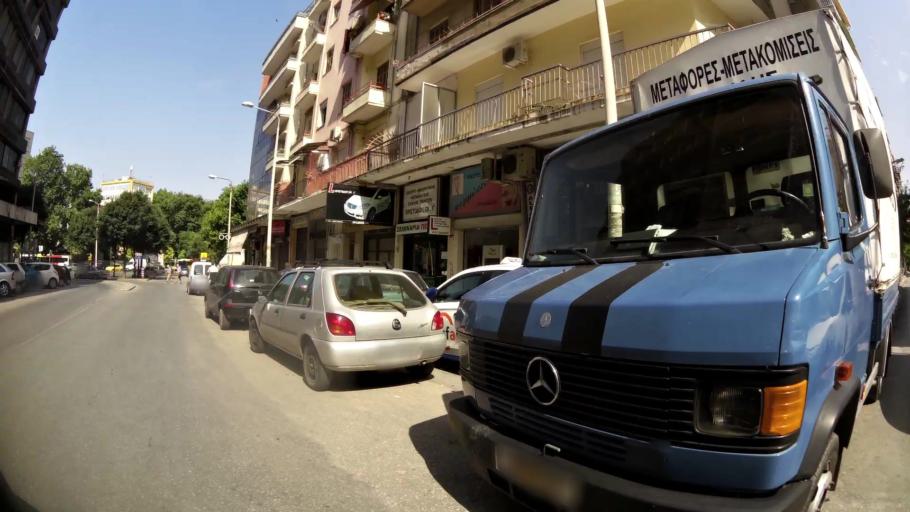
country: GR
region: Central Macedonia
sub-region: Nomos Thessalonikis
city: Thessaloniki
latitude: 40.6405
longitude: 22.9368
